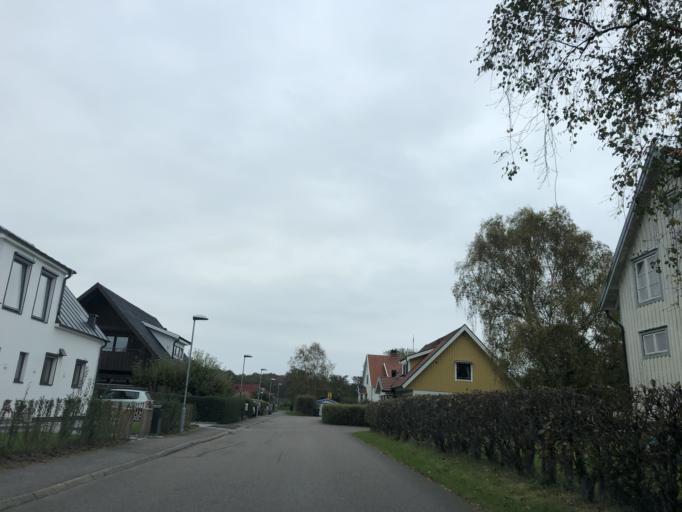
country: SE
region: Vaestra Goetaland
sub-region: Goteborg
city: Majorna
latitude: 57.6547
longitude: 11.8760
